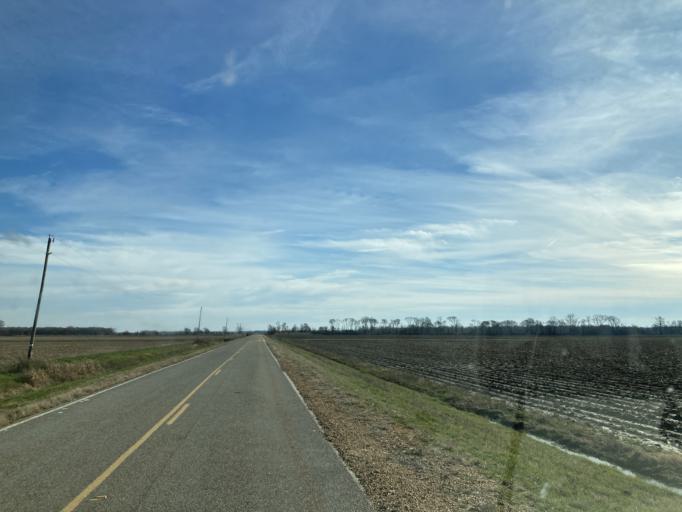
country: US
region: Mississippi
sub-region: Humphreys County
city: Belzoni
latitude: 33.0229
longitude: -90.6209
